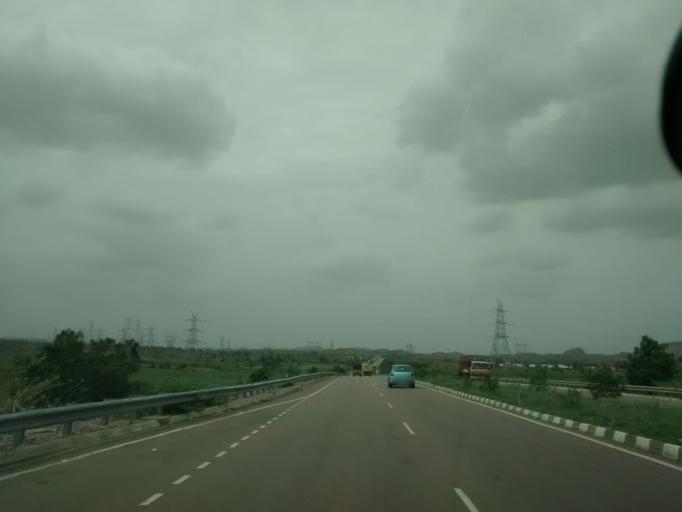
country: IN
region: Andhra Pradesh
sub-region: Kurnool
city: Ramapuram
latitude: 15.1356
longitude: 77.6621
